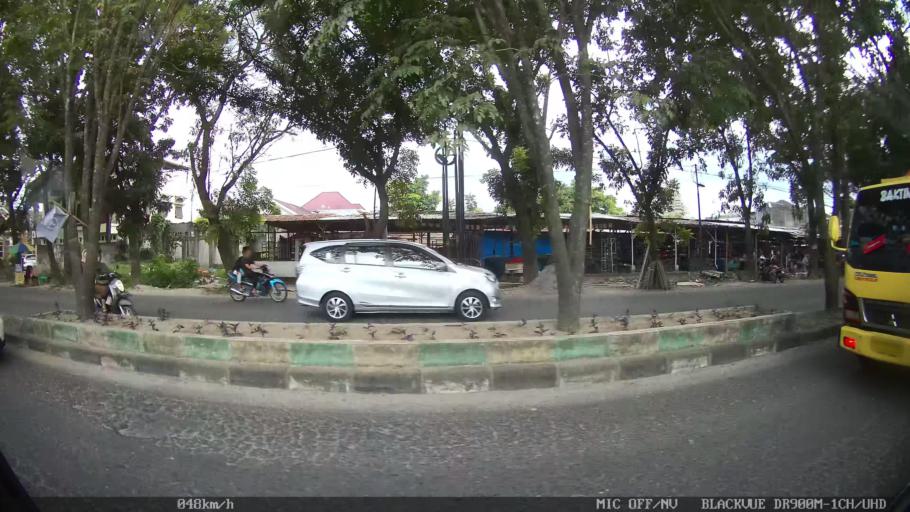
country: ID
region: North Sumatra
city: Sunggal
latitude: 3.5492
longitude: 98.6081
